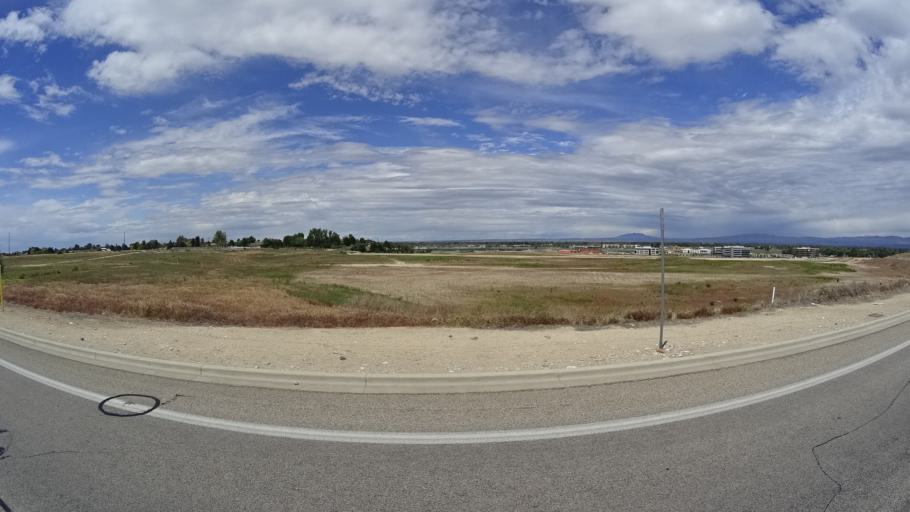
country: US
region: Idaho
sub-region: Ada County
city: Meridian
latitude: 43.5852
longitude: -116.4303
